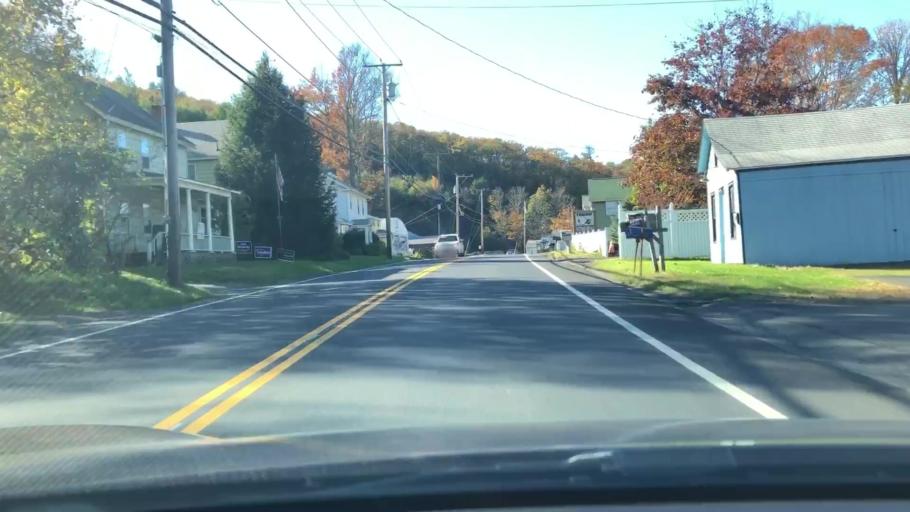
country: US
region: New York
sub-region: Ulster County
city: Saugerties
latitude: 42.0802
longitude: -73.9921
